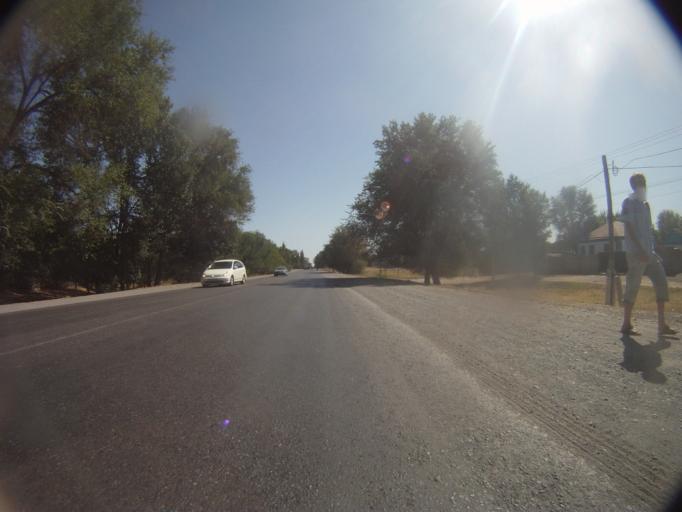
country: KG
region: Chuy
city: Kara-Balta
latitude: 42.8420
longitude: 73.9371
